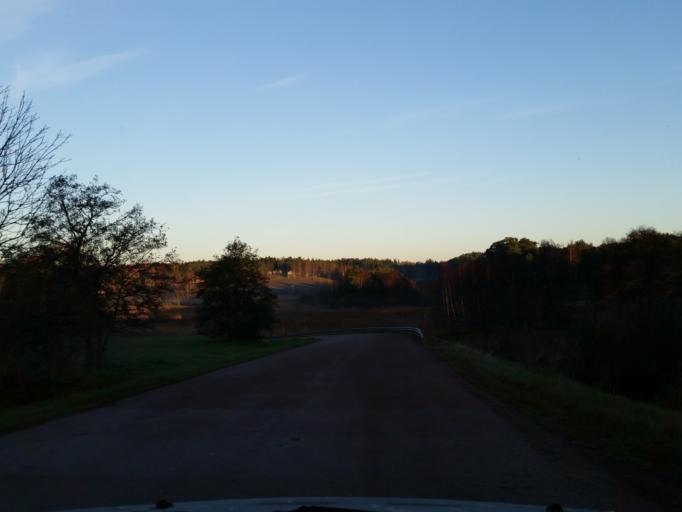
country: AX
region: Alands landsbygd
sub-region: Sund
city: Sund
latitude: 60.2313
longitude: 20.0850
